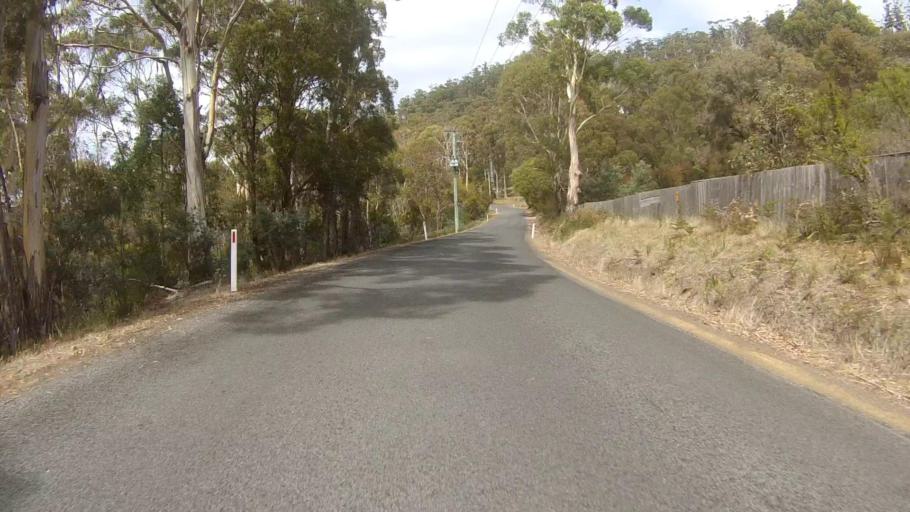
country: AU
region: Tasmania
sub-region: Kingborough
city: Blackmans Bay
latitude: -43.0236
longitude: 147.3234
